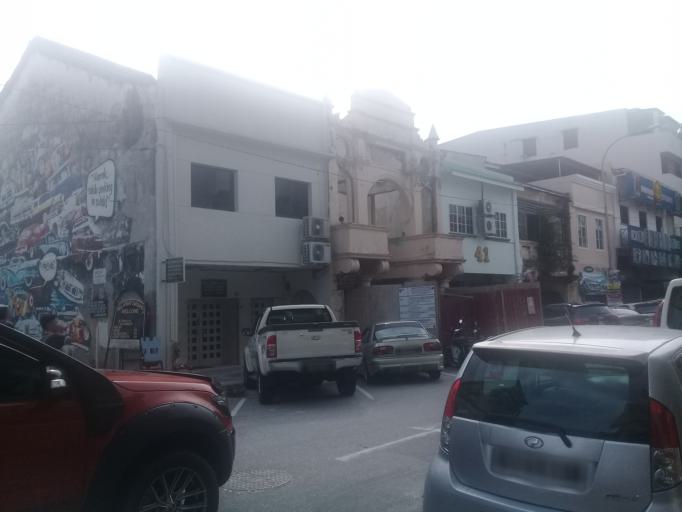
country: MY
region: Perak
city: Ipoh
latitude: 4.5965
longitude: 101.0783
